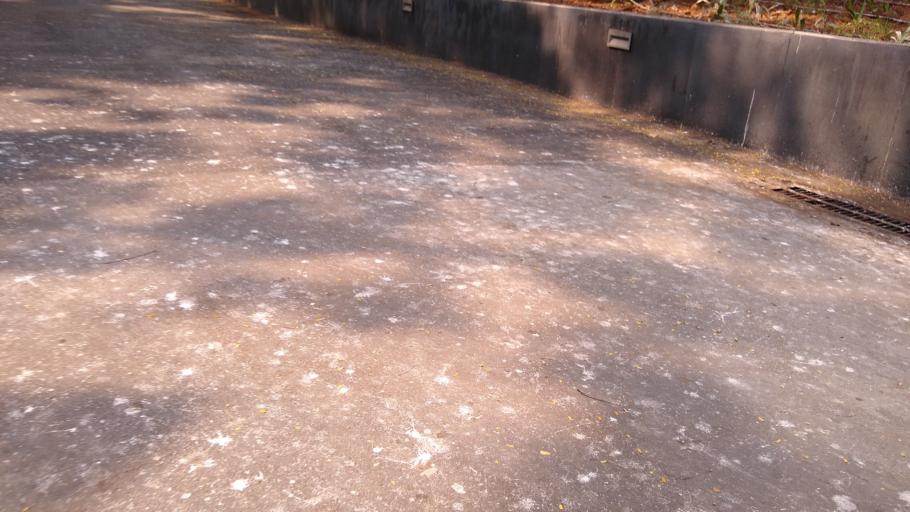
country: IN
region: Maharashtra
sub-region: Mumbai Suburban
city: Powai
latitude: 19.1519
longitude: 72.8550
